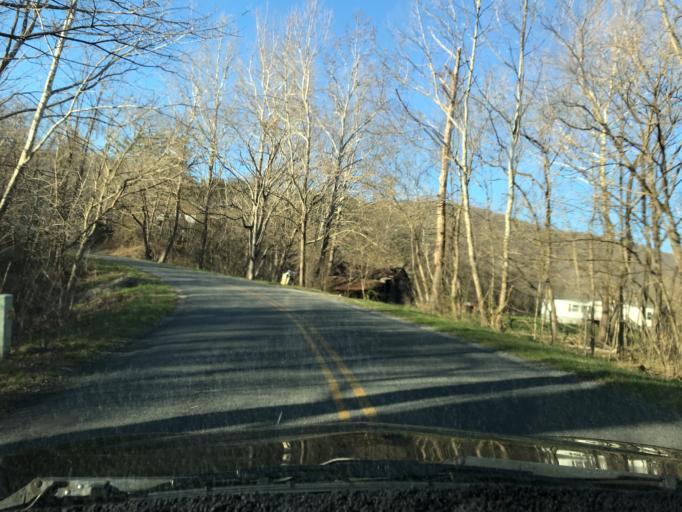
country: US
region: Virginia
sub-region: Botetourt County
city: Buchanan
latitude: 37.4626
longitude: -79.6594
